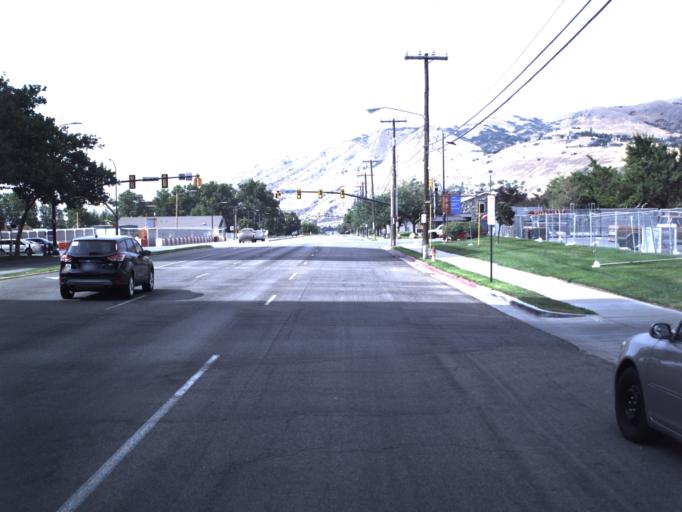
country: US
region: Utah
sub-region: Salt Lake County
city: Salt Lake City
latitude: 40.7706
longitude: -111.8996
